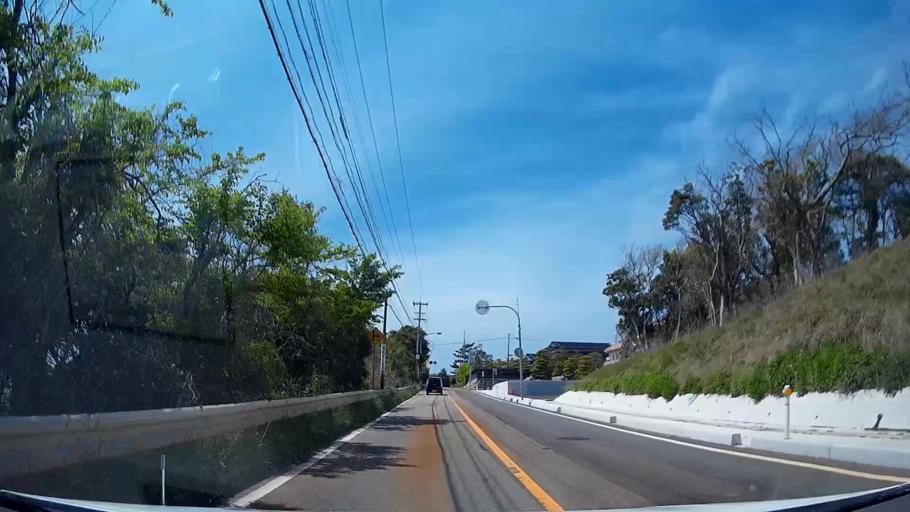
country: JP
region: Ishikawa
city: Hakui
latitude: 36.9245
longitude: 136.7639
